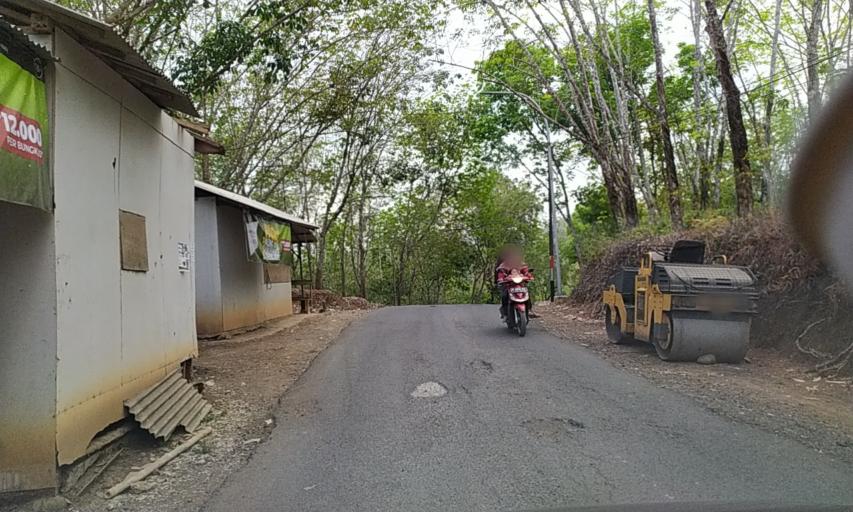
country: ID
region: Central Java
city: Cigalumpit
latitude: -7.3084
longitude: 108.5937
